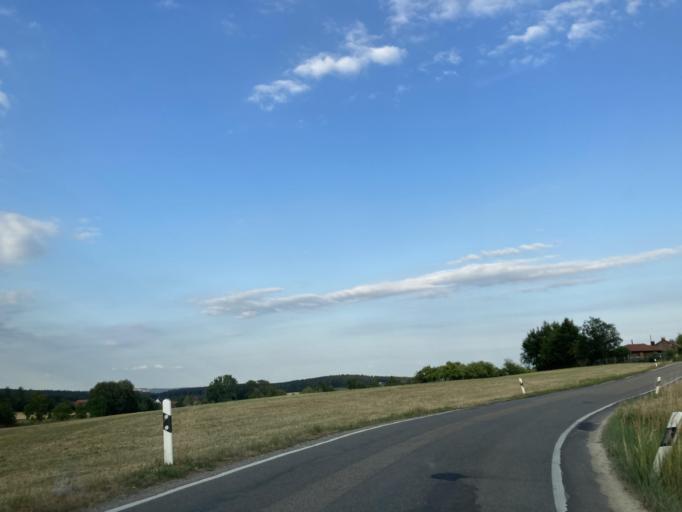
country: DE
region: Baden-Wuerttemberg
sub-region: Karlsruhe Region
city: Ebhausen
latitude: 48.6222
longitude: 8.6520
